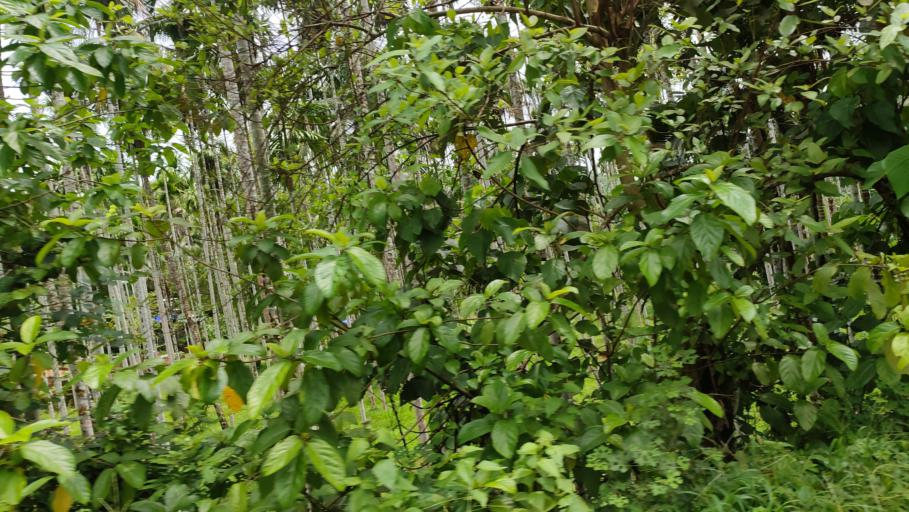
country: IN
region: Kerala
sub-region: Kasaragod District
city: Nileshwar
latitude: 12.2958
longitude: 75.2830
